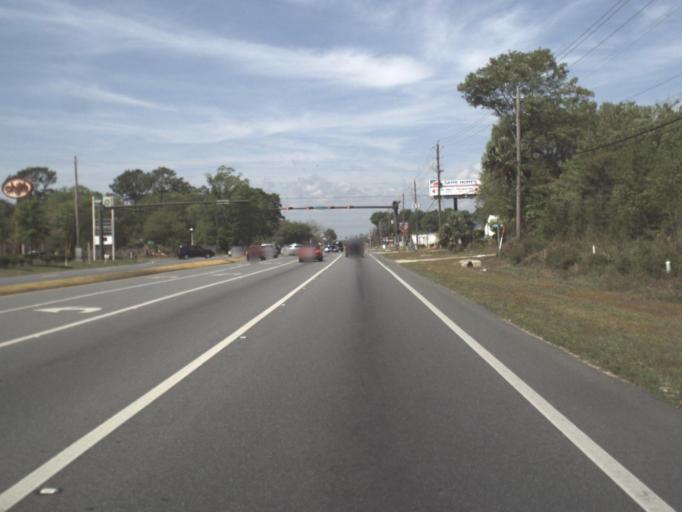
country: US
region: Florida
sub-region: Santa Rosa County
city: Pace
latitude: 30.6036
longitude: -87.1265
